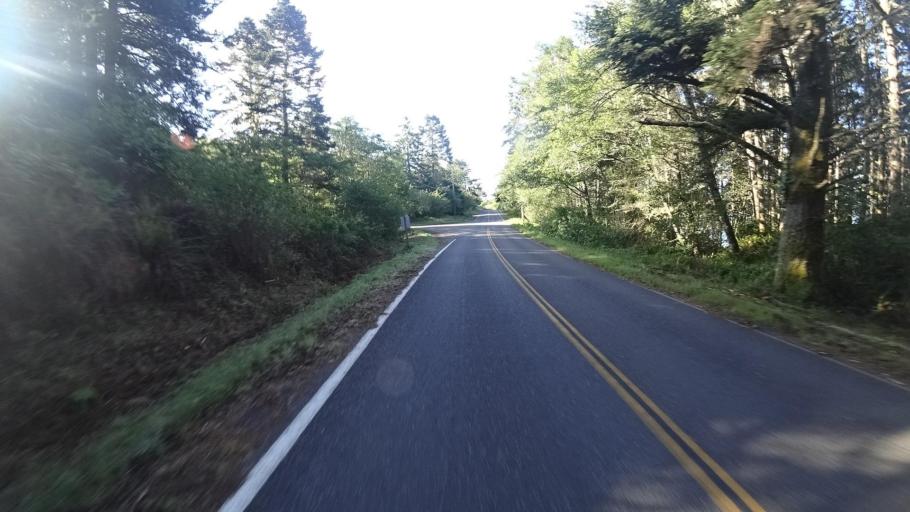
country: US
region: California
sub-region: Humboldt County
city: Westhaven-Moonstone
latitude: 41.0979
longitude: -124.1577
